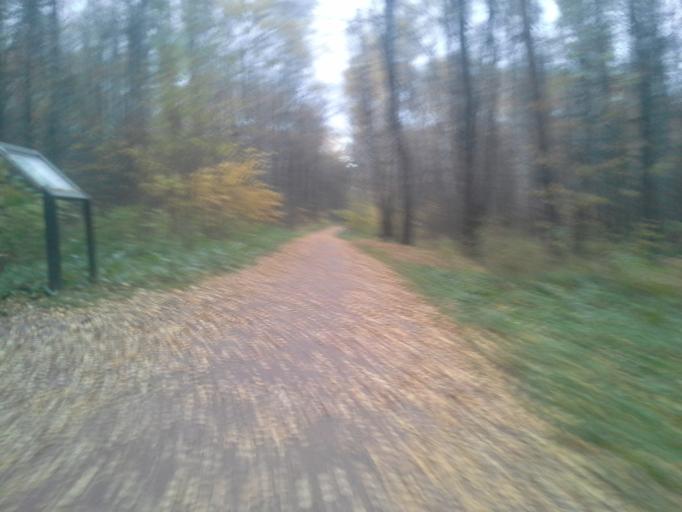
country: RU
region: Moskovskaya
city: Zarech'ye
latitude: 55.6657
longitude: 37.3985
